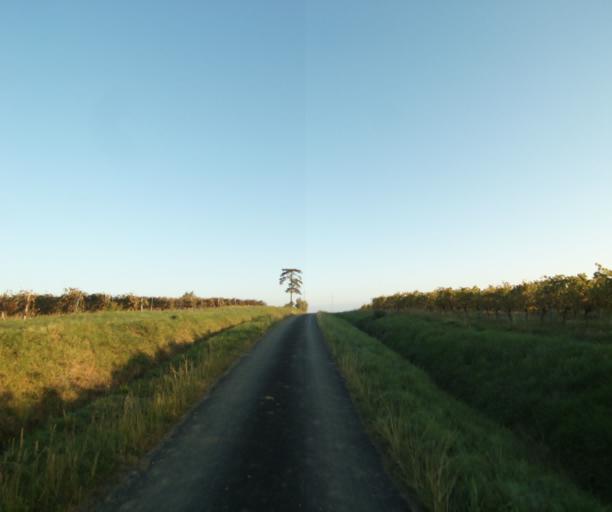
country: FR
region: Midi-Pyrenees
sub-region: Departement du Gers
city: Gondrin
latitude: 43.7793
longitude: 0.1863
